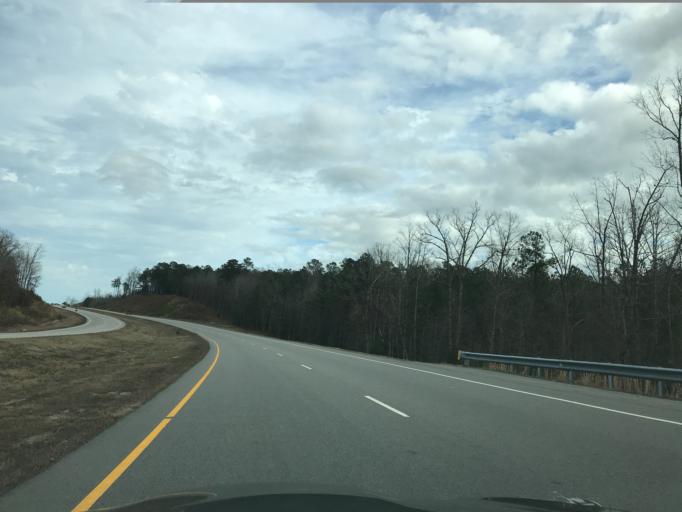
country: US
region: North Carolina
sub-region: Wake County
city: Rolesville
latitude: 35.8991
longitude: -78.4717
